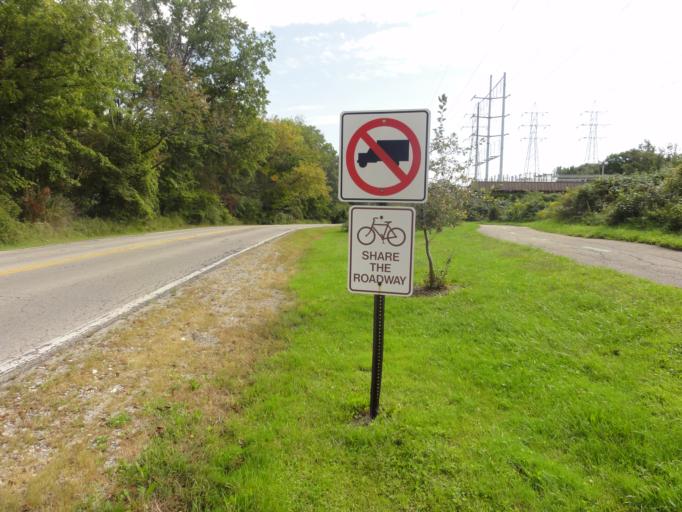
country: US
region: Ohio
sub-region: Cuyahoga County
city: Berea
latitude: 41.3540
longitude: -81.8579
